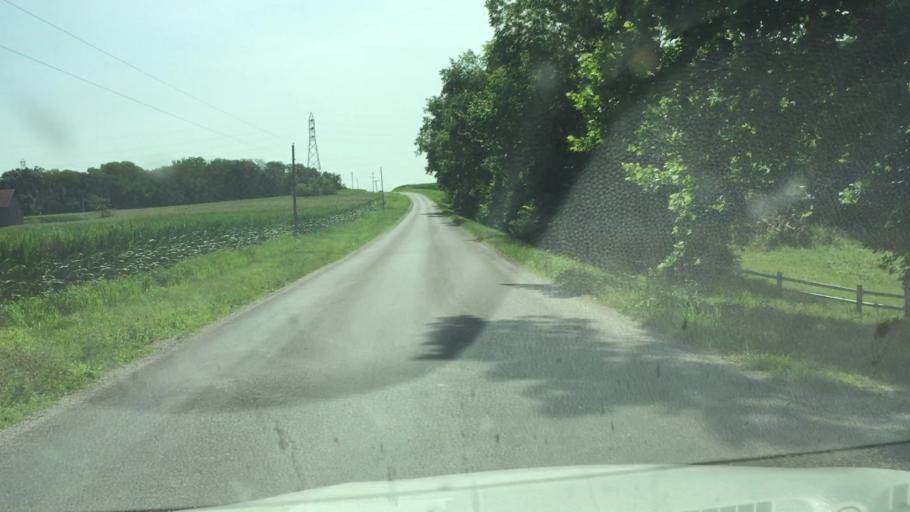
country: US
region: Illinois
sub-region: Hancock County
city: Nauvoo
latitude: 40.5121
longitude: -91.3549
